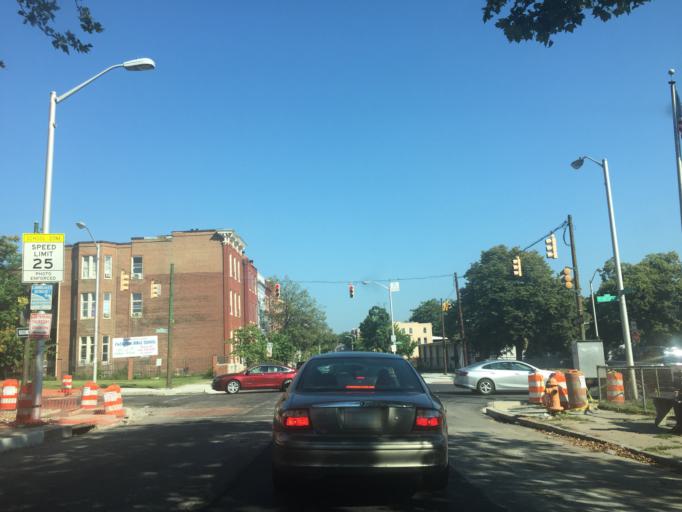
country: US
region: Maryland
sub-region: City of Baltimore
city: Baltimore
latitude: 39.3048
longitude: -76.6305
